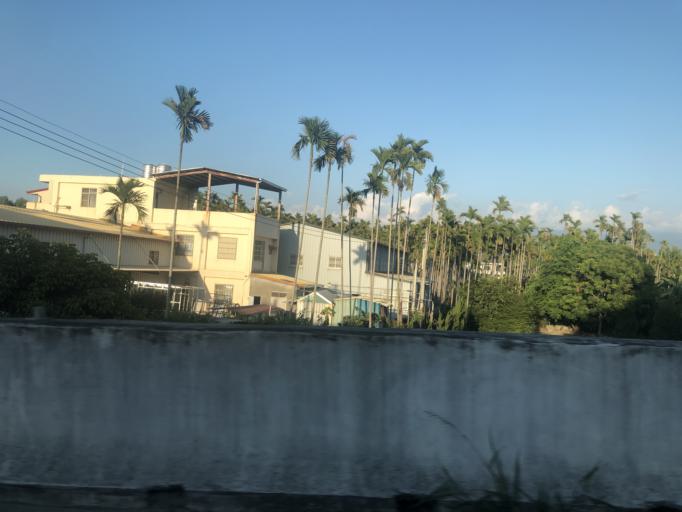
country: TW
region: Taiwan
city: Fengyuan
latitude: 24.2781
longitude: 120.7776
